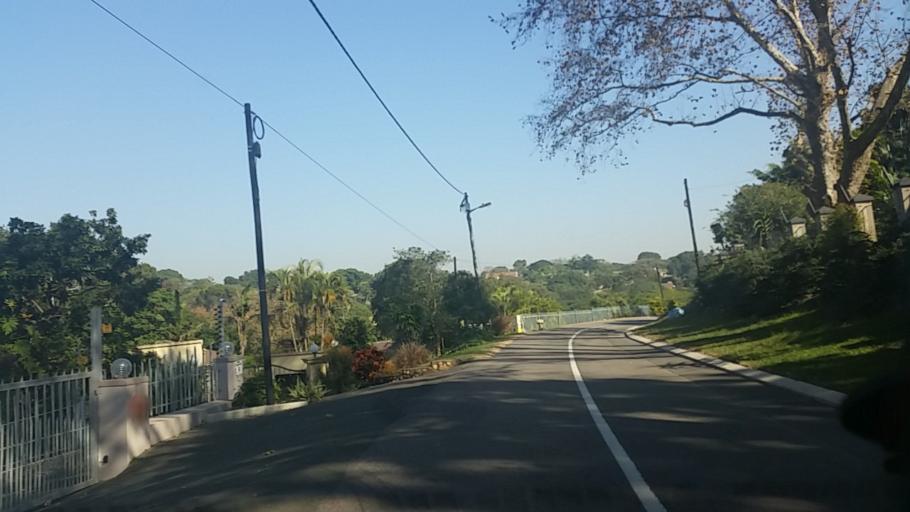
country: ZA
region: KwaZulu-Natal
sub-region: eThekwini Metropolitan Municipality
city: Berea
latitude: -29.8410
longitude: 30.9108
